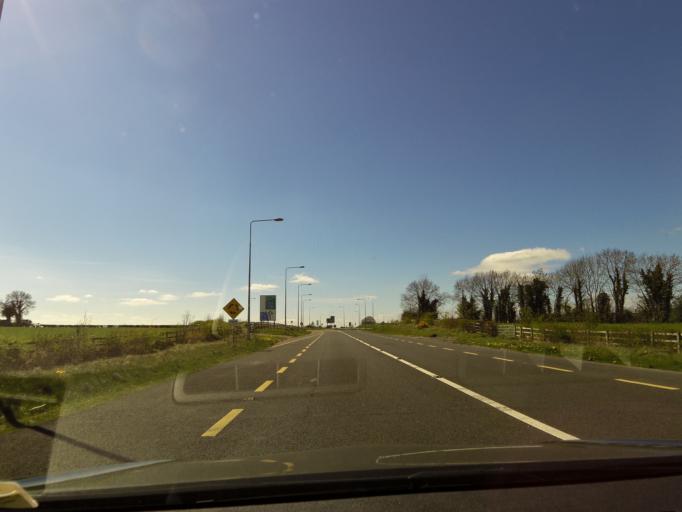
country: IE
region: Leinster
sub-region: Kildare
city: Moone
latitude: 52.9987
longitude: -6.8384
